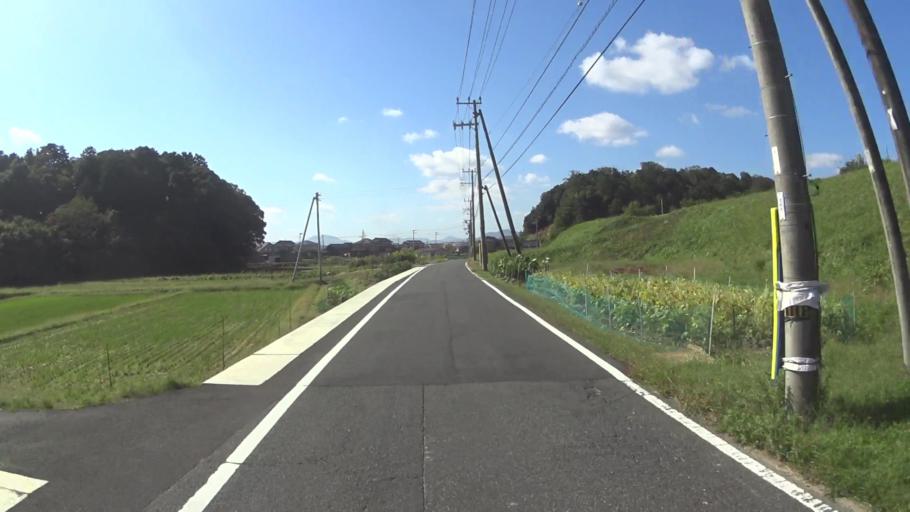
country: JP
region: Kyoto
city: Miyazu
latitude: 35.6847
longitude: 135.0933
